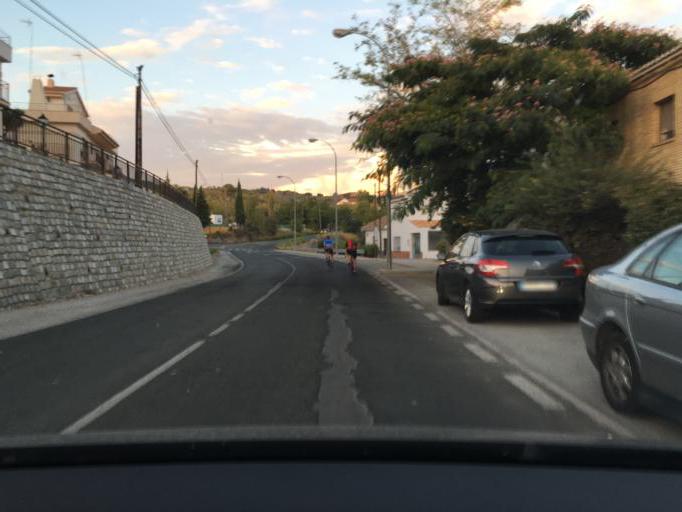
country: ES
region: Andalusia
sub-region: Provincia de Granada
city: Viznar
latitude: 37.2099
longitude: -3.5560
